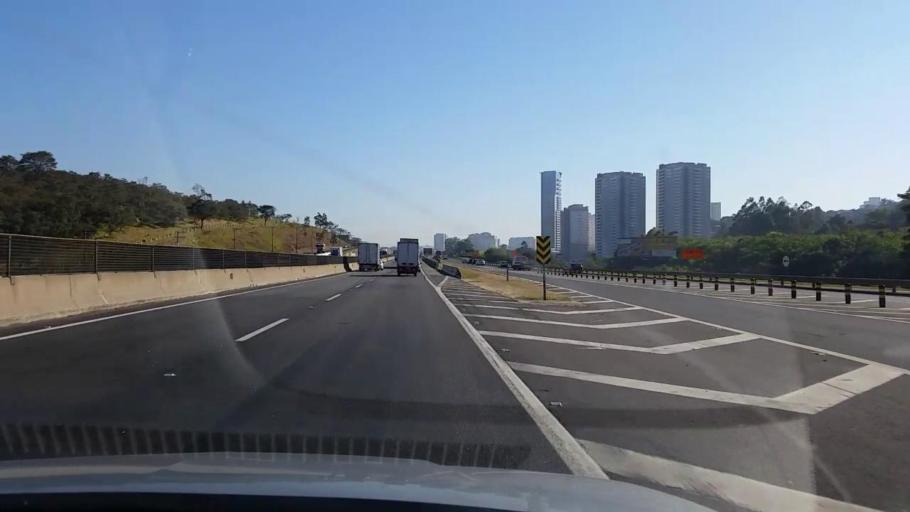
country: BR
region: Sao Paulo
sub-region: Jundiai
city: Jundiai
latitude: -23.2012
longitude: -46.9021
